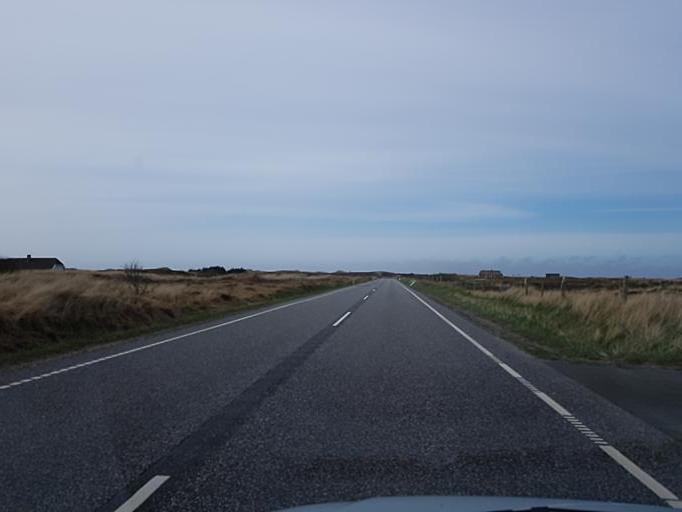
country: DK
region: Central Jutland
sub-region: Ringkobing-Skjern Kommune
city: Hvide Sande
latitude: 55.8883
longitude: 8.1742
